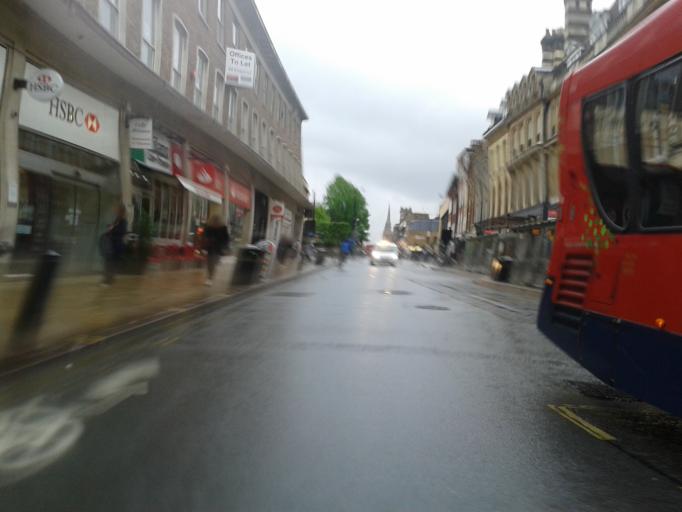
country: GB
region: England
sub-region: Cambridgeshire
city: Cambridge
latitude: 52.2047
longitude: 0.1225
